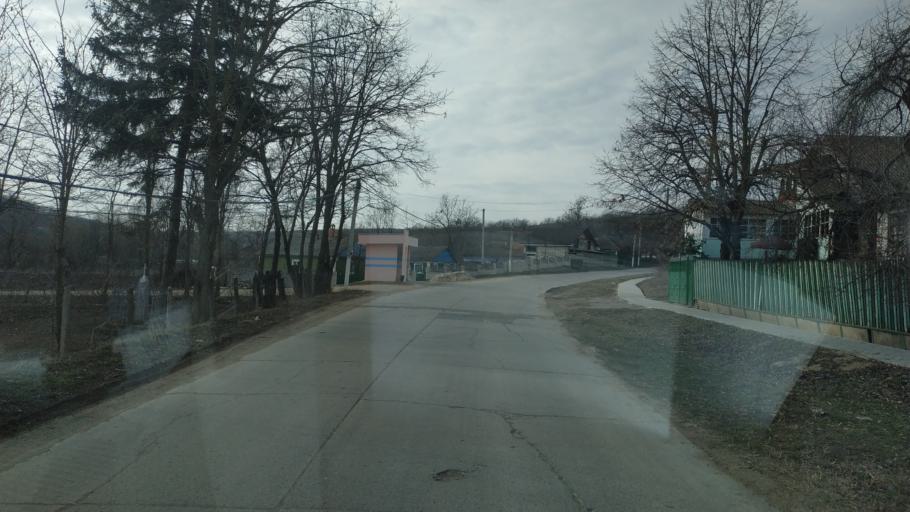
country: MD
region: Chisinau
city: Vadul lui Voda
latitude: 47.0069
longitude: 29.1248
